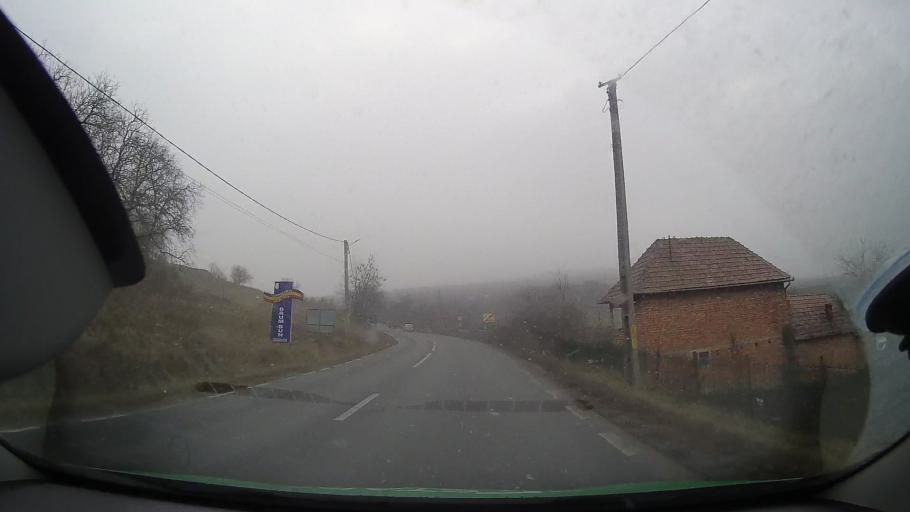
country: RO
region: Sibiu
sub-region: Comuna Blajel
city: Blajel
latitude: 46.1968
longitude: 24.3243
